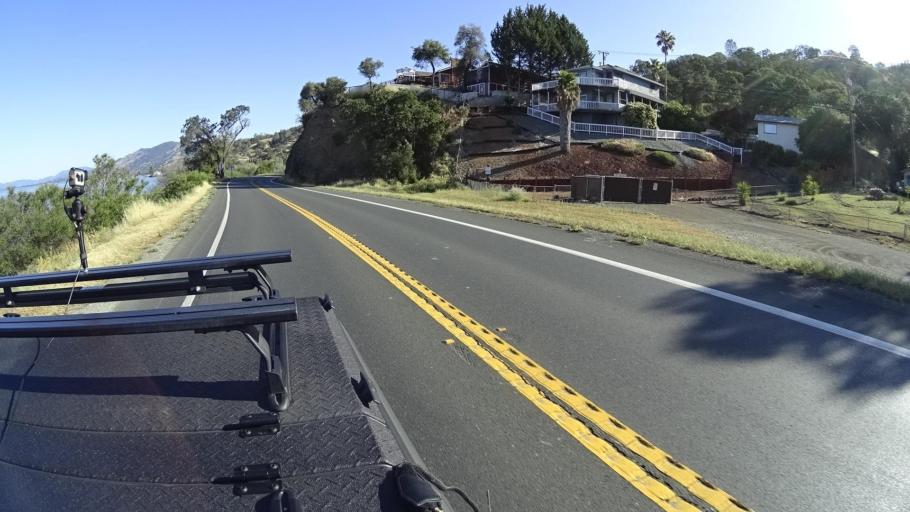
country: US
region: California
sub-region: Lake County
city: Lucerne
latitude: 39.0720
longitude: -122.7821
